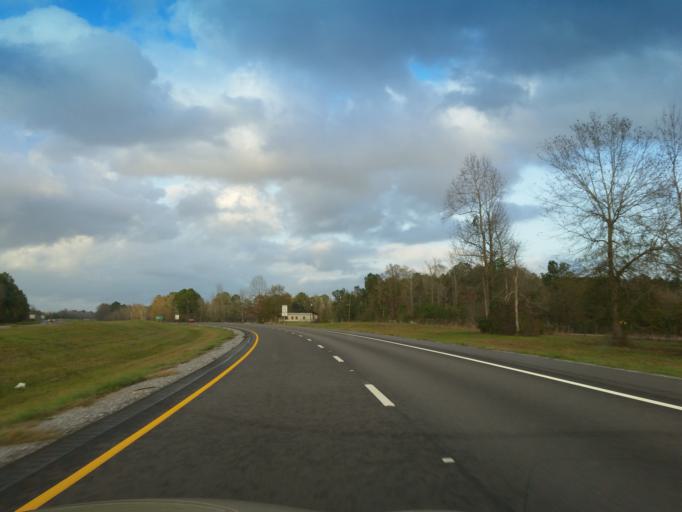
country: US
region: Mississippi
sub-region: Jones County
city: Sharon
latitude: 31.9111
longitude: -89.0086
